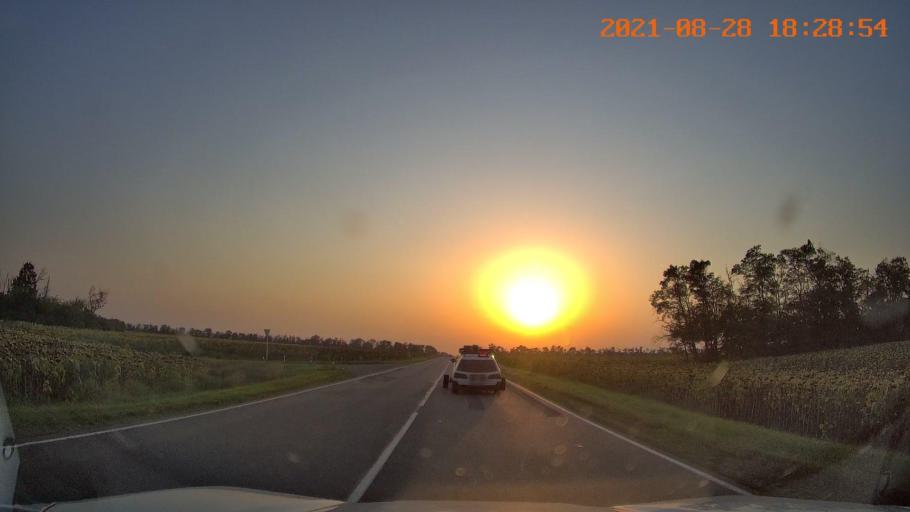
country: RU
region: Adygeya
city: Dondukovskaya
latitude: 44.8797
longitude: 40.2602
